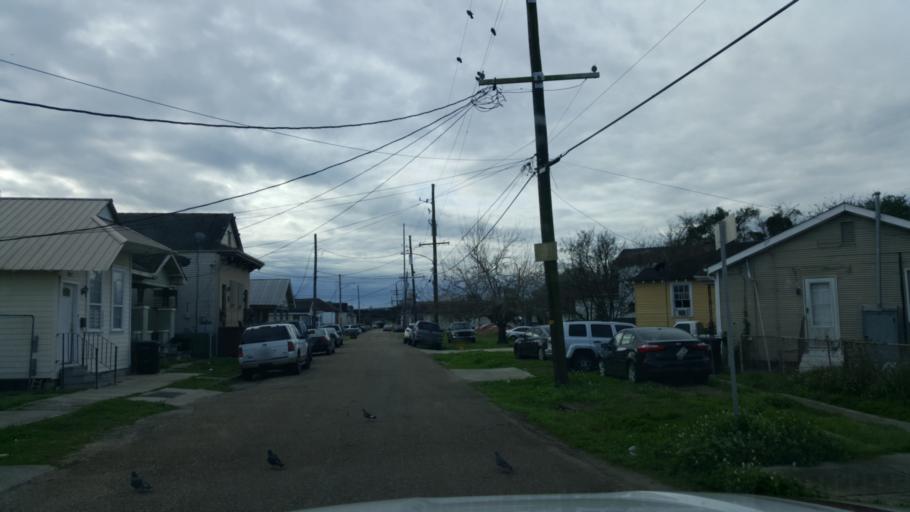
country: US
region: Louisiana
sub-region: Orleans Parish
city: New Orleans
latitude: 29.9772
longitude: -90.0646
